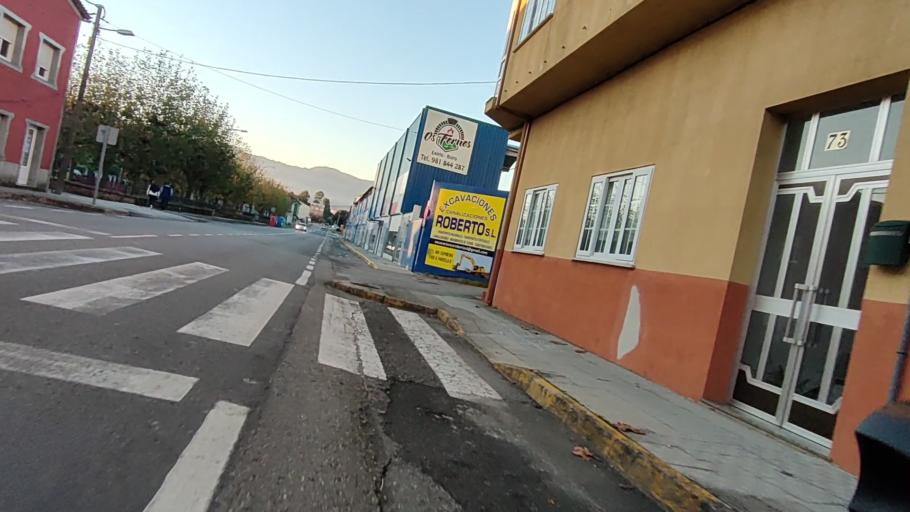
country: ES
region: Galicia
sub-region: Provincia da Coruna
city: Boiro
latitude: 42.6384
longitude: -8.8785
